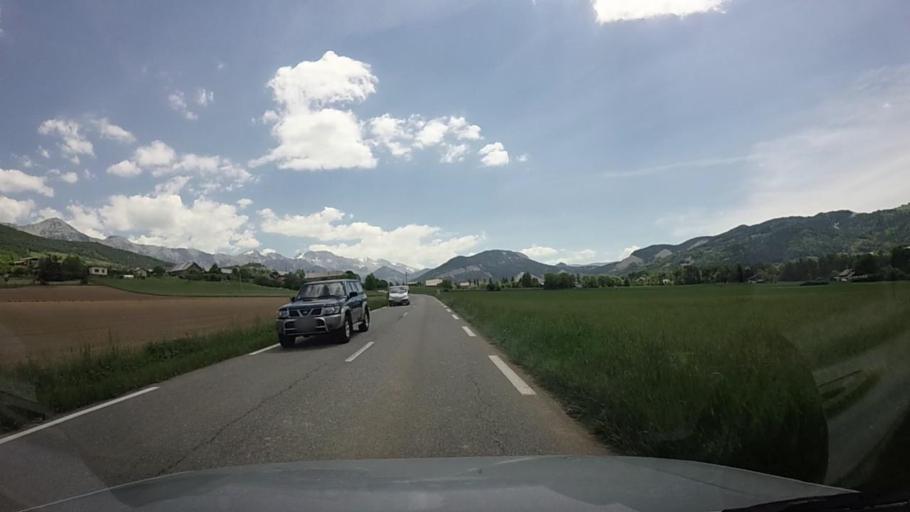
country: FR
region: Provence-Alpes-Cote d'Azur
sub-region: Departement des Alpes-de-Haute-Provence
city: Seyne-les-Alpes
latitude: 44.3584
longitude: 6.3325
